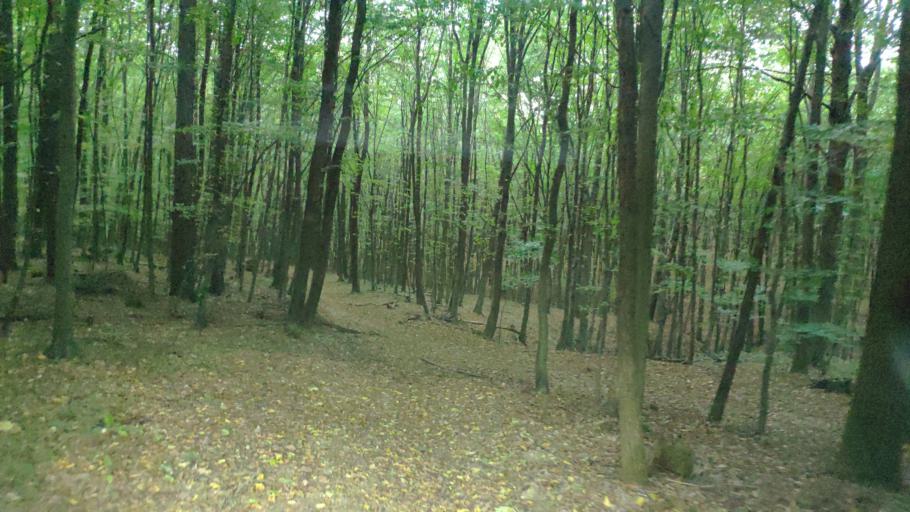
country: SK
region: Kosicky
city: Kosice
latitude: 48.6989
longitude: 21.1990
